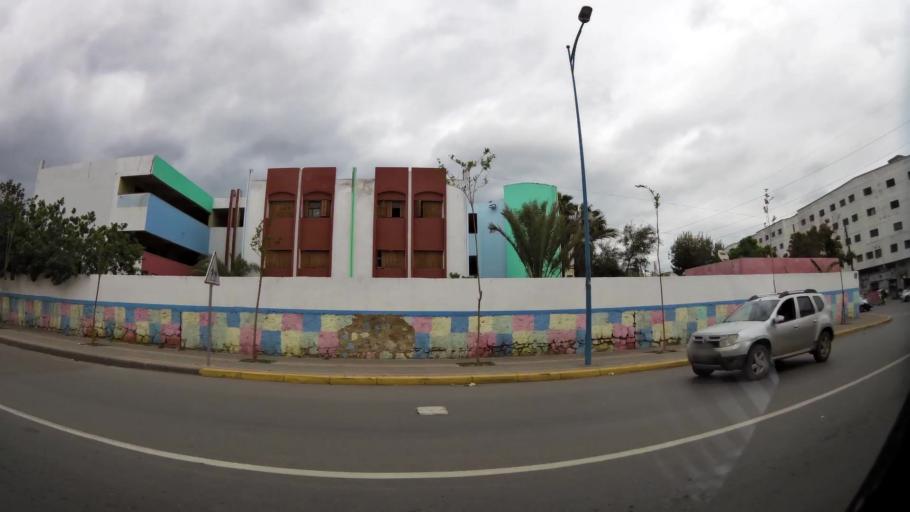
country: MA
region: Grand Casablanca
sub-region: Casablanca
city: Casablanca
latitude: 33.5984
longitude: -7.5459
